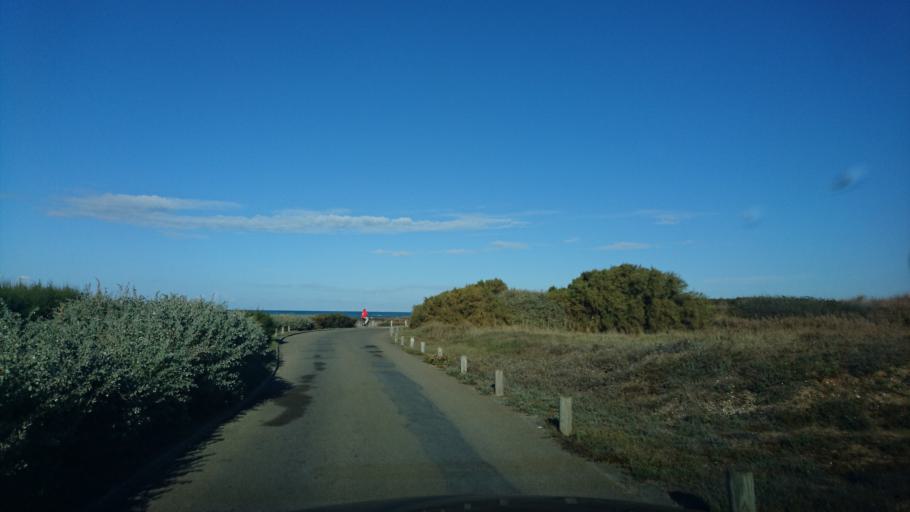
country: FR
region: Pays de la Loire
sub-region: Departement de la Vendee
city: Les Sables-d'Olonne
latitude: 46.5059
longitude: -1.8165
